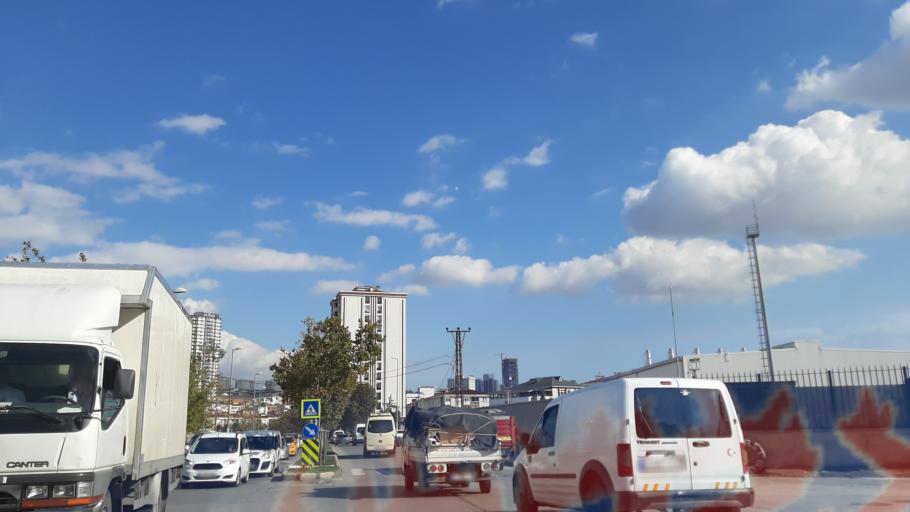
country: TR
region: Istanbul
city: Esenyurt
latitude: 41.0308
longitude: 28.6605
